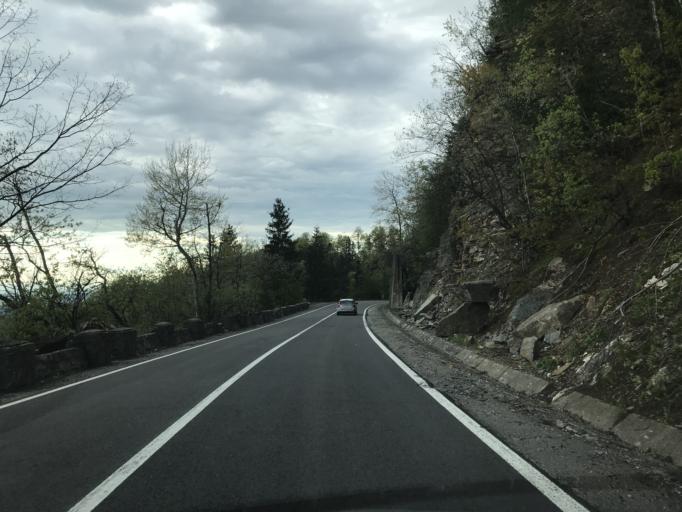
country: RO
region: Sibiu
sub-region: Comuna Cartisoara
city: Cartisoara
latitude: 45.6595
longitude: 24.5981
